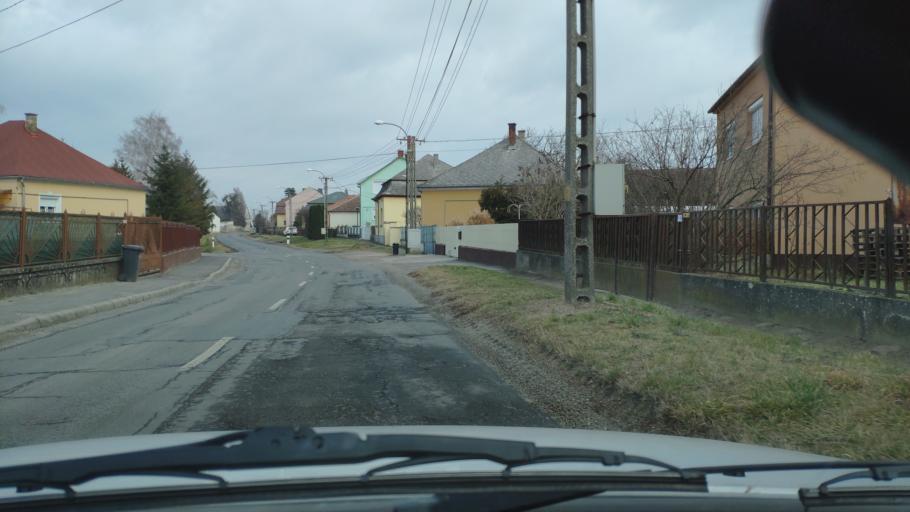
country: HU
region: Zala
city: Nagykanizsa
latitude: 46.4542
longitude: 16.9515
